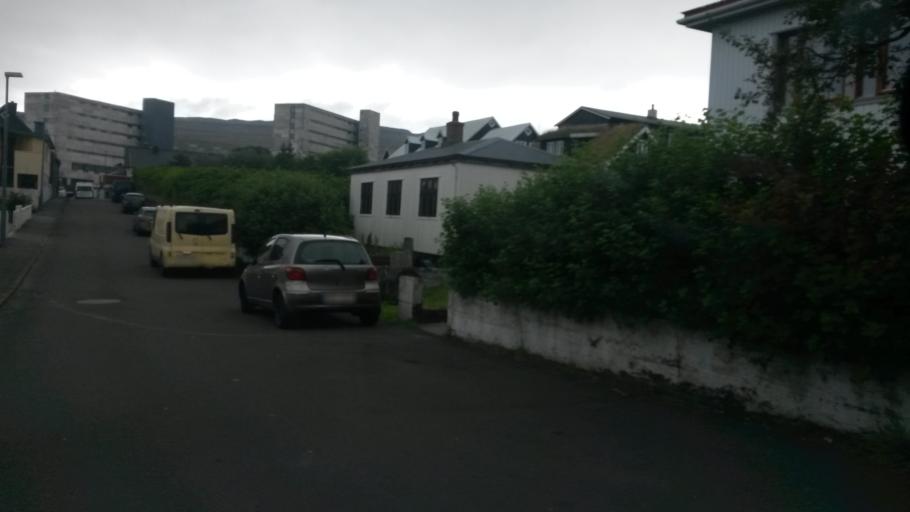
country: FO
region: Streymoy
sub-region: Torshavn
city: Torshavn
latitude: 62.0052
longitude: -6.7787
